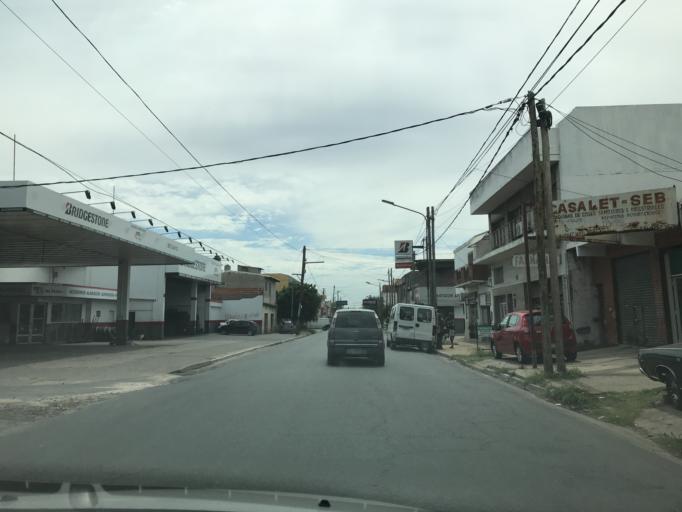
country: AR
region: Buenos Aires
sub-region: Partido de Lomas de Zamora
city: Lomas de Zamora
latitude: -34.7305
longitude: -58.4245
